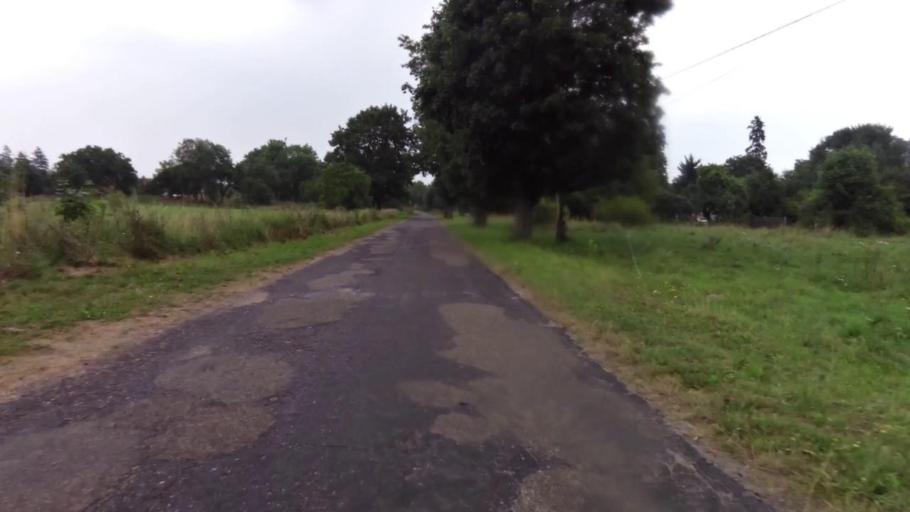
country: PL
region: West Pomeranian Voivodeship
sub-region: Powiat lobeski
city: Wegorzyno
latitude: 53.5371
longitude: 15.6699
